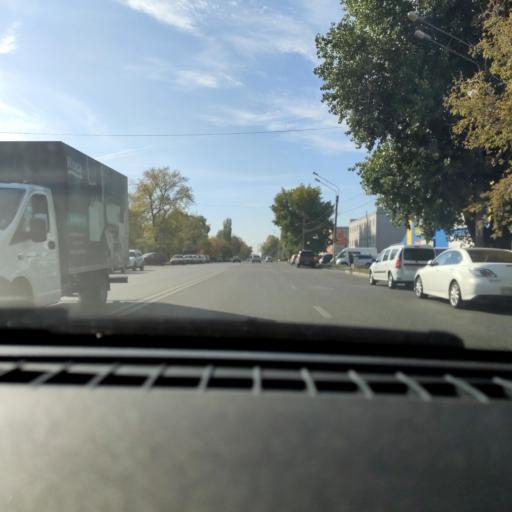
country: RU
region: Voronezj
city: Voronezh
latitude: 51.6533
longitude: 39.2718
